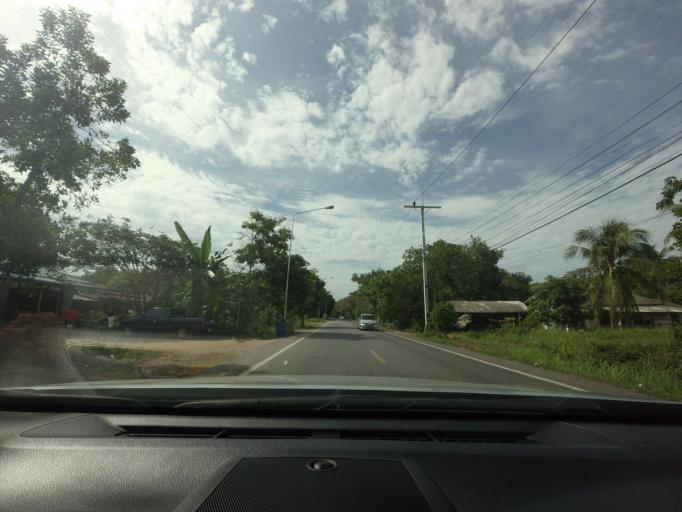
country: TH
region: Songkhla
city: Khlong Hoi Khong
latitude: 6.9012
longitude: 100.4143
